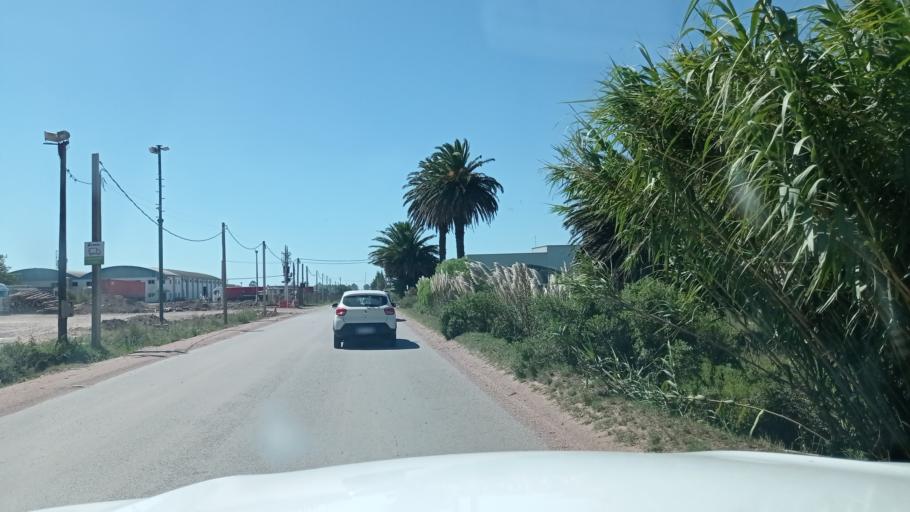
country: UY
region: Montevideo
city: Pajas Blancas
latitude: -34.8661
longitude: -56.2875
